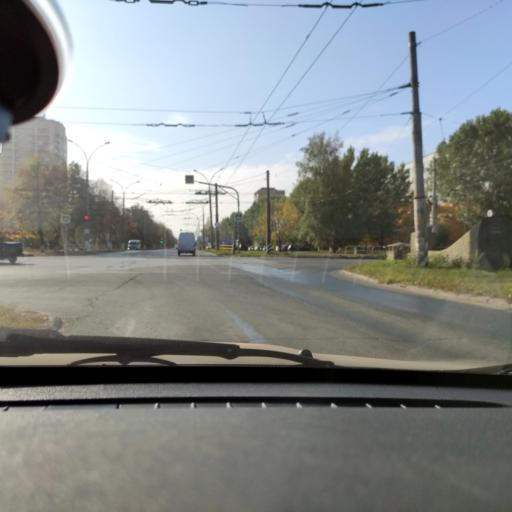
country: RU
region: Samara
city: Tol'yatti
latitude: 53.5384
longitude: 49.2784
